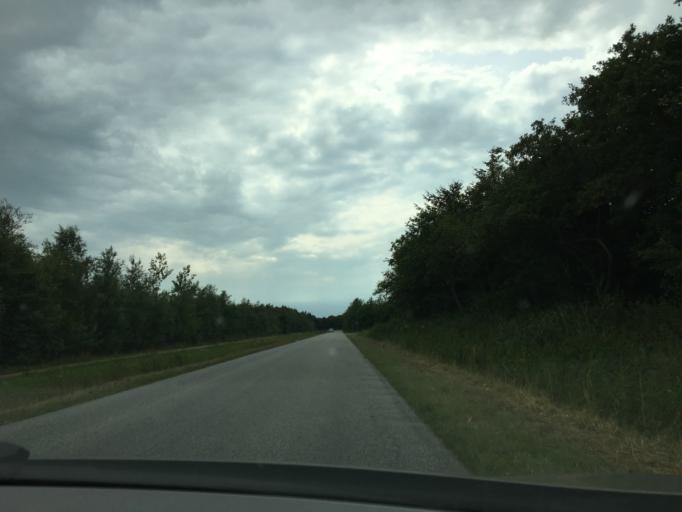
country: DK
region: South Denmark
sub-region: Varde Kommune
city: Oksbol
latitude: 55.8371
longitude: 8.2857
